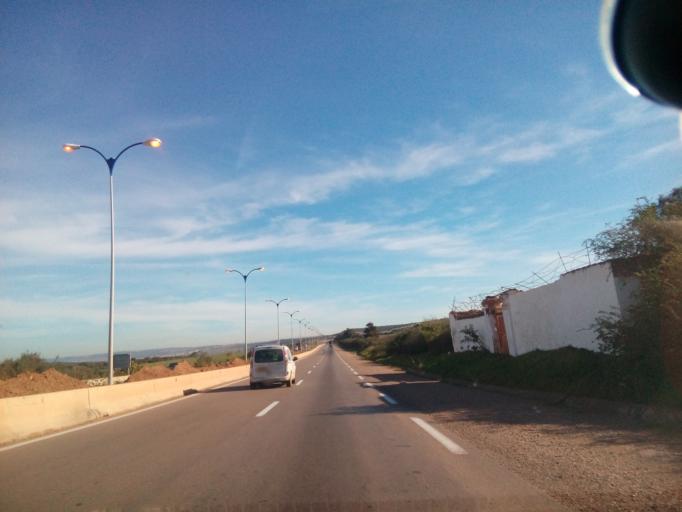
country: DZ
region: Mostaganem
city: Mostaganem
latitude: 35.8027
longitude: -0.0646
